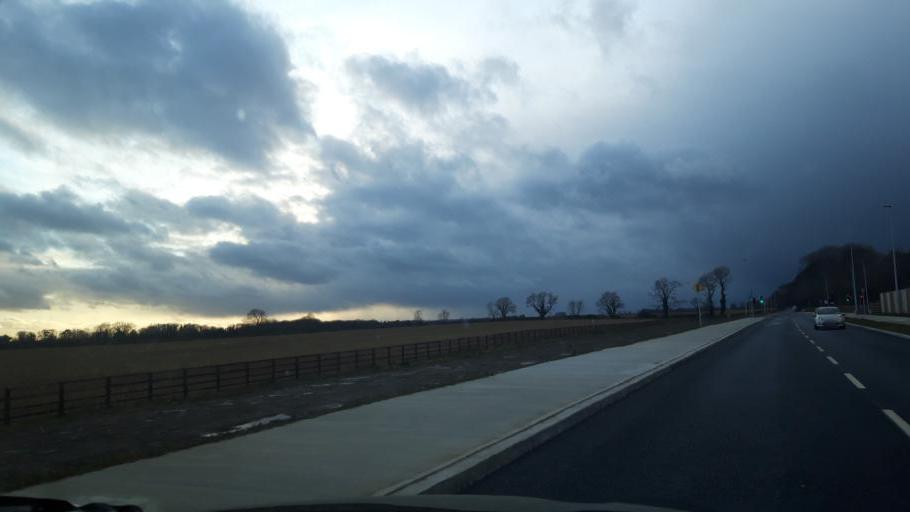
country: IE
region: Leinster
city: Donabate
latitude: 53.4793
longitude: -6.1646
